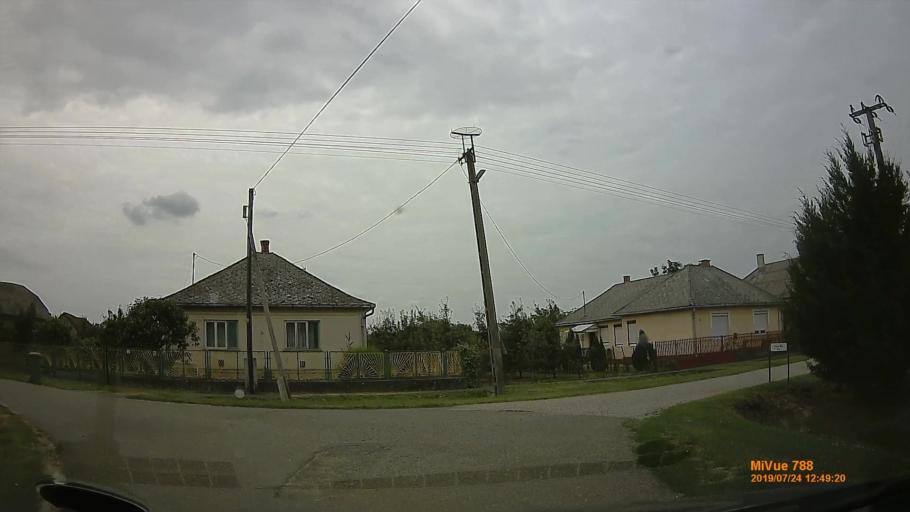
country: HU
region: Szabolcs-Szatmar-Bereg
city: Aranyosapati
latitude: 48.1907
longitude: 22.3123
